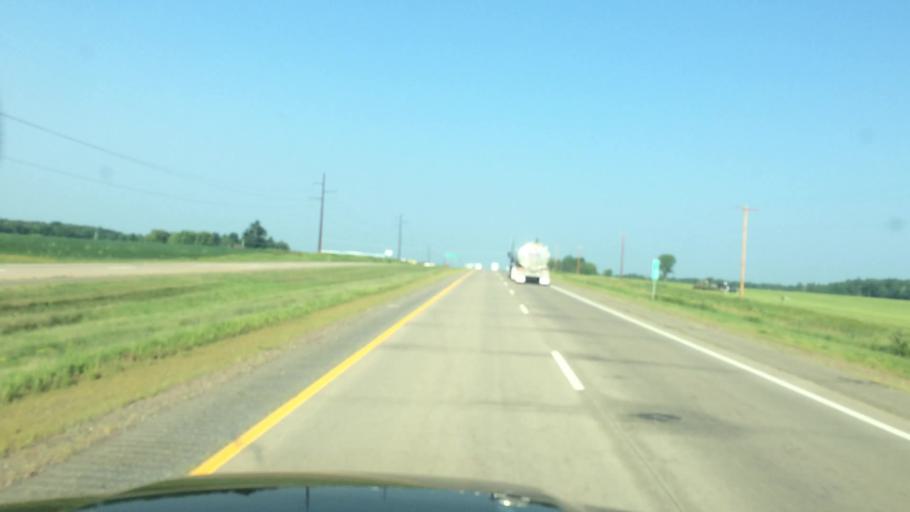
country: US
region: Wisconsin
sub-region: Marathon County
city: Edgar
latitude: 44.9444
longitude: -89.9984
